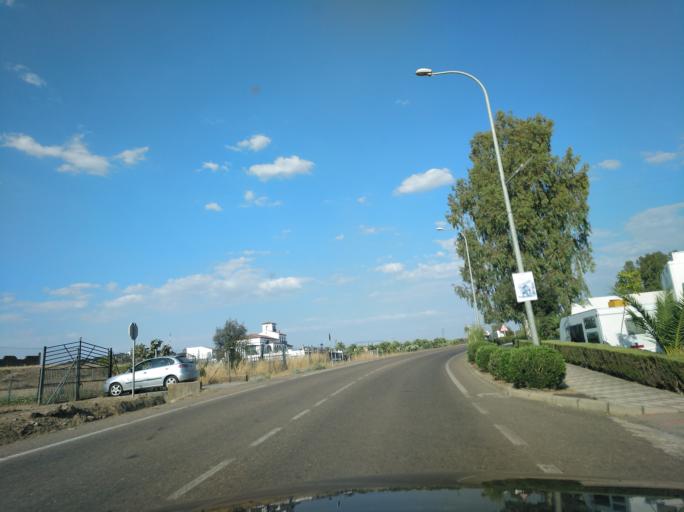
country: ES
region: Extremadura
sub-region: Provincia de Badajoz
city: Villanueva del Fresno
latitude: 38.3804
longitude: -7.1649
